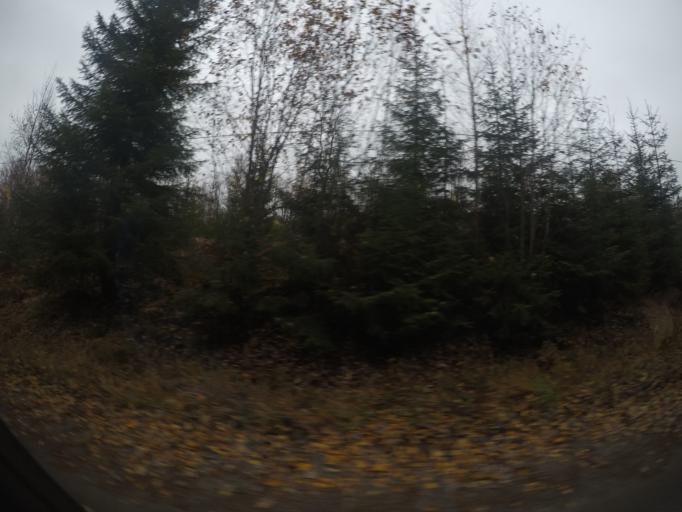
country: SE
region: Vaestmanland
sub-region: Surahammars Kommun
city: Ramnas
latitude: 59.7175
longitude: 16.0925
